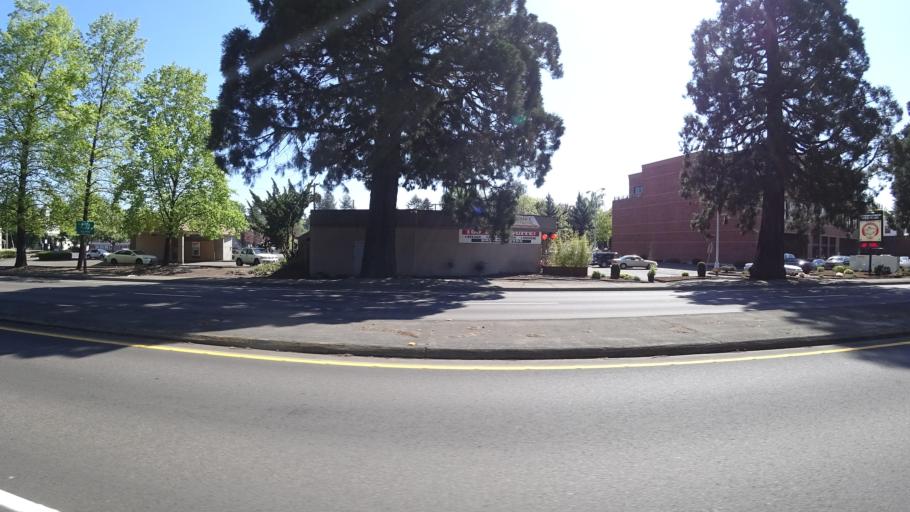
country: US
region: Oregon
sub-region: Clackamas County
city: Milwaukie
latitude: 45.4473
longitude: -122.6428
